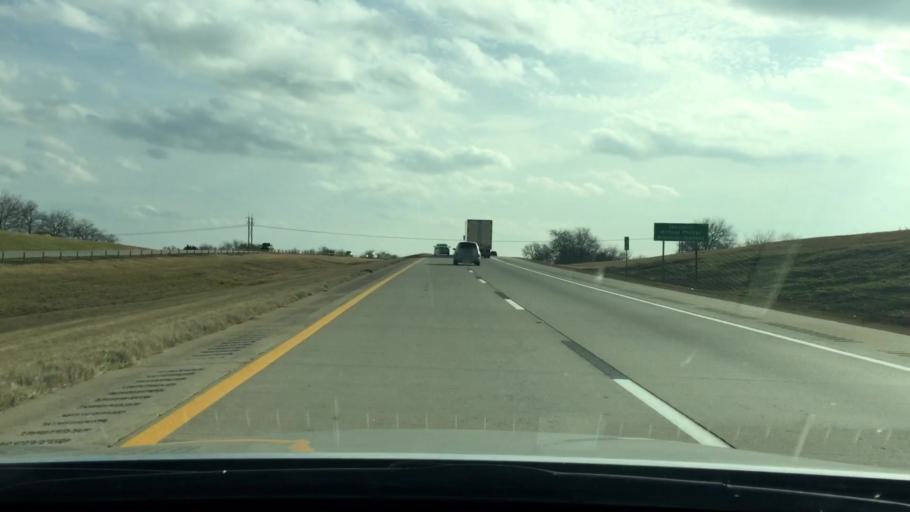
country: US
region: Oklahoma
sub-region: Carter County
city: Ardmore
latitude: 34.2359
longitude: -97.1621
